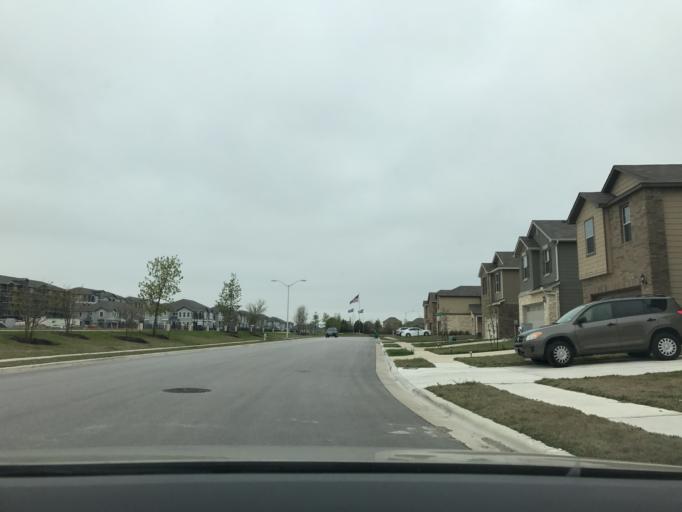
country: US
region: Texas
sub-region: Travis County
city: Wells Branch
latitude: 30.4667
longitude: -97.6825
